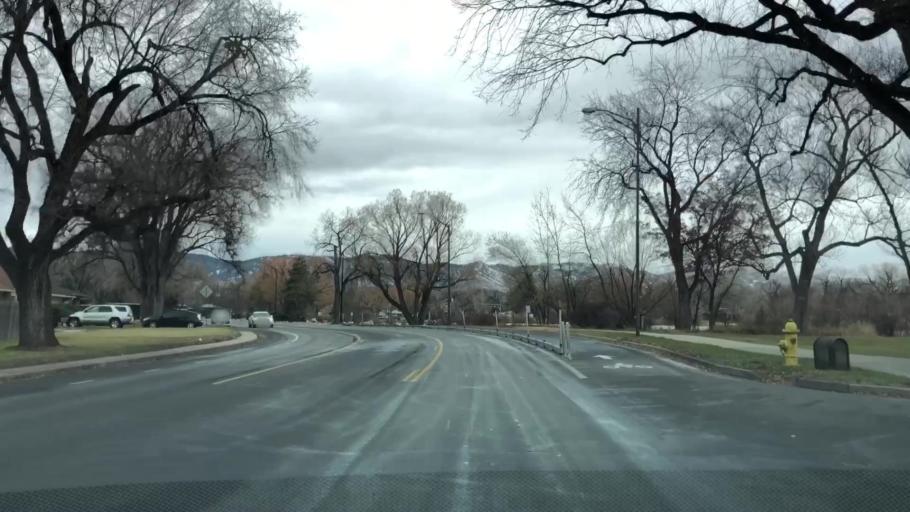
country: US
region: Colorado
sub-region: Larimer County
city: Fort Collins
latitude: 40.5819
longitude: -105.1019
